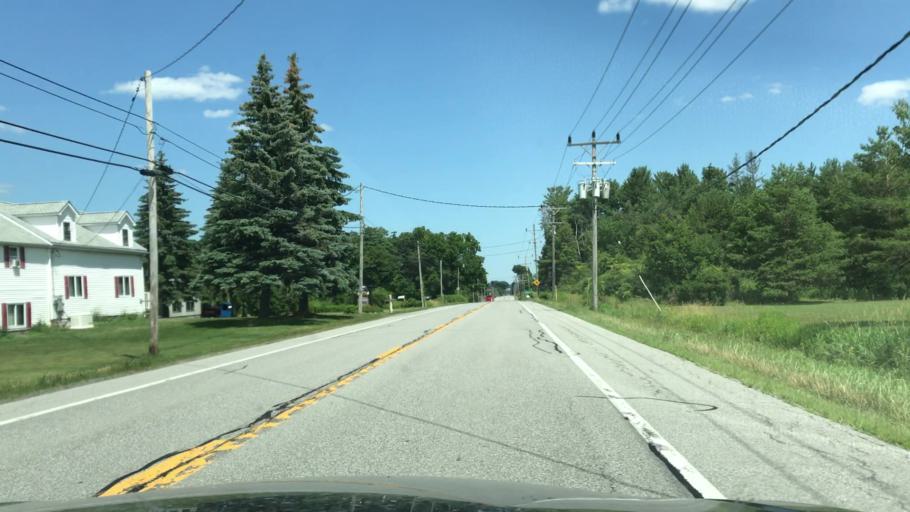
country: US
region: New York
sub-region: Wyoming County
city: Perry
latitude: 42.7446
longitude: -78.0541
